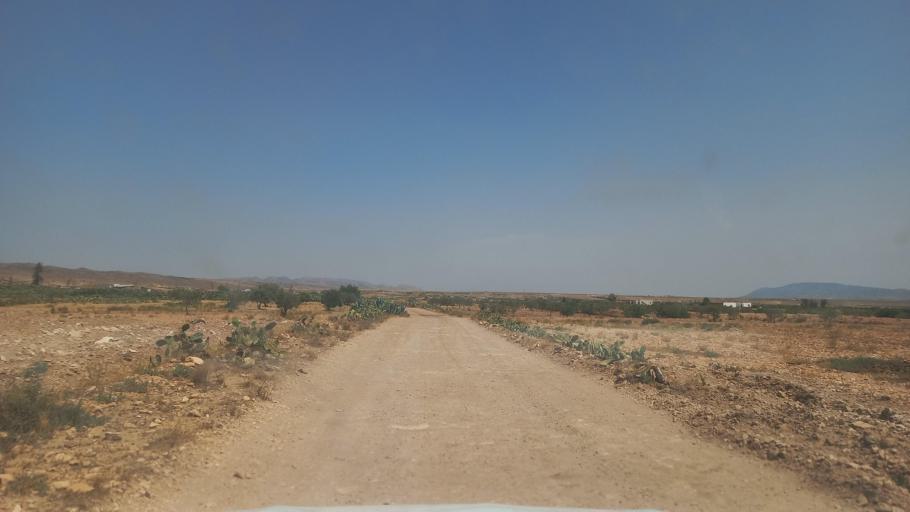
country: TN
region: Al Qasrayn
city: Kasserine
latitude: 35.2811
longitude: 8.9484
